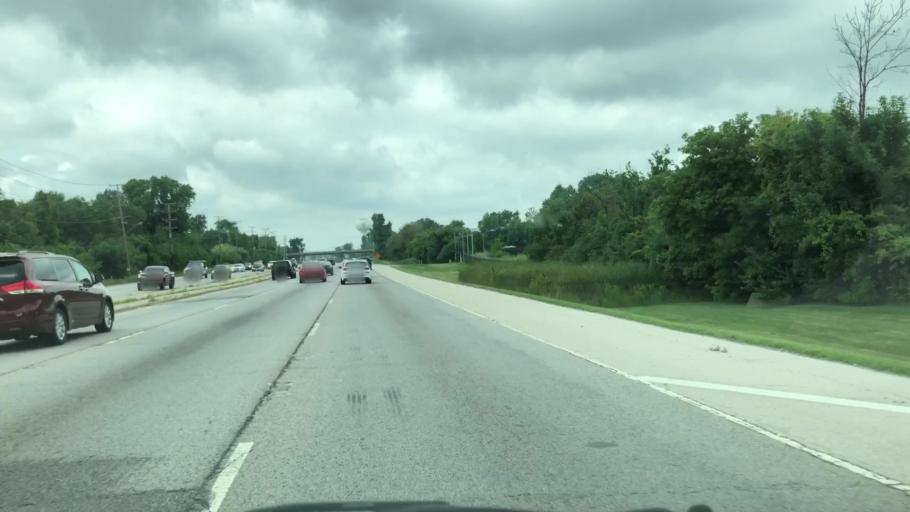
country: US
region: Illinois
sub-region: DuPage County
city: Elmhurst
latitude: 41.8816
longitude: -87.9614
